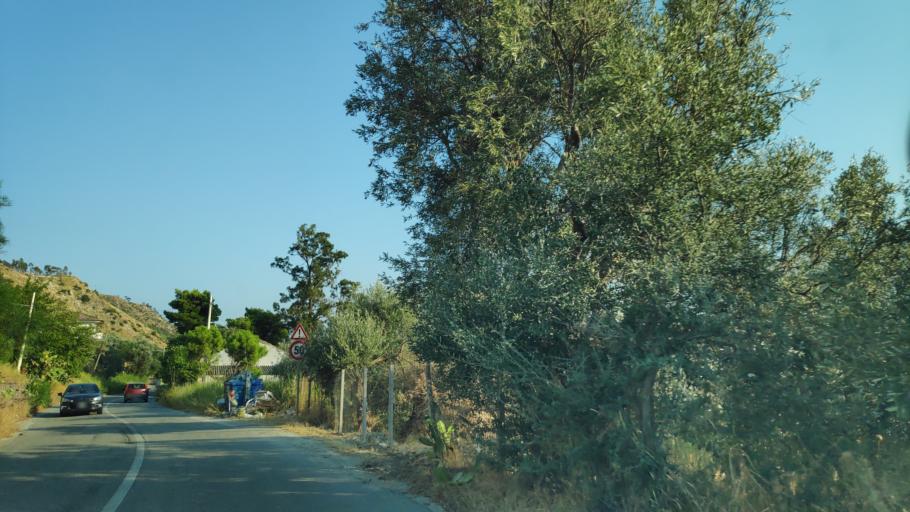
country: IT
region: Calabria
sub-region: Provincia di Reggio Calabria
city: Caulonia
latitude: 38.3813
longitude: 16.4367
